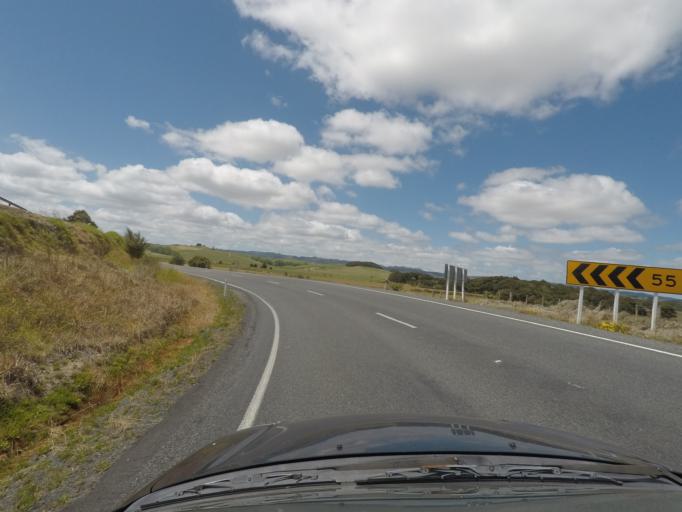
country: NZ
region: Northland
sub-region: Whangarei
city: Ruakaka
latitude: -35.9898
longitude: 174.4565
